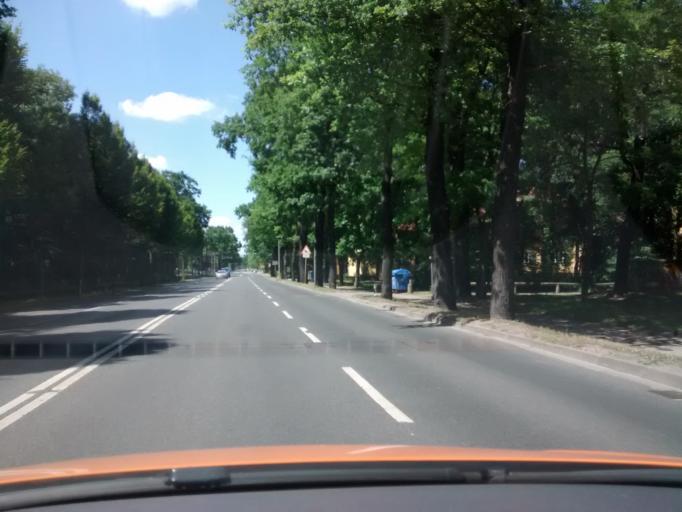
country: DE
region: Brandenburg
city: Potsdam
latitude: 52.3750
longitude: 13.0869
